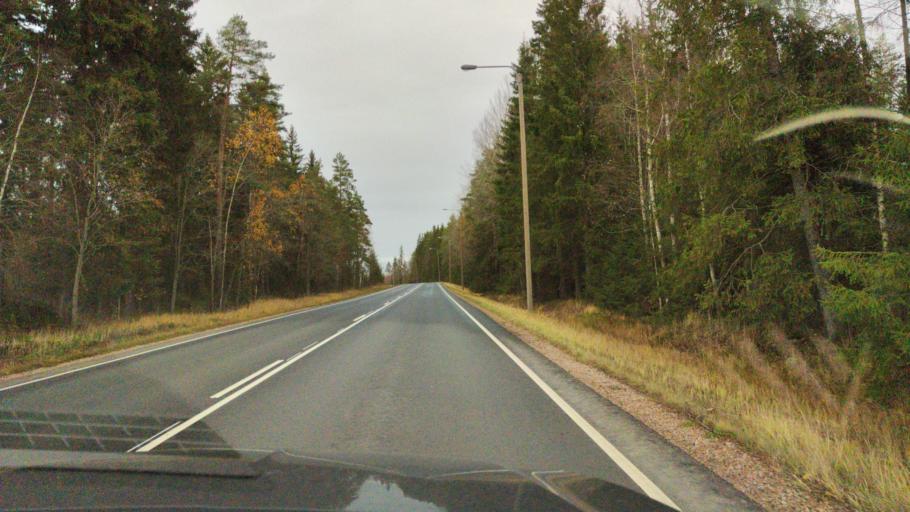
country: FI
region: Varsinais-Suomi
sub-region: Turku
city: Vahto
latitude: 60.6602
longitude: 22.4335
